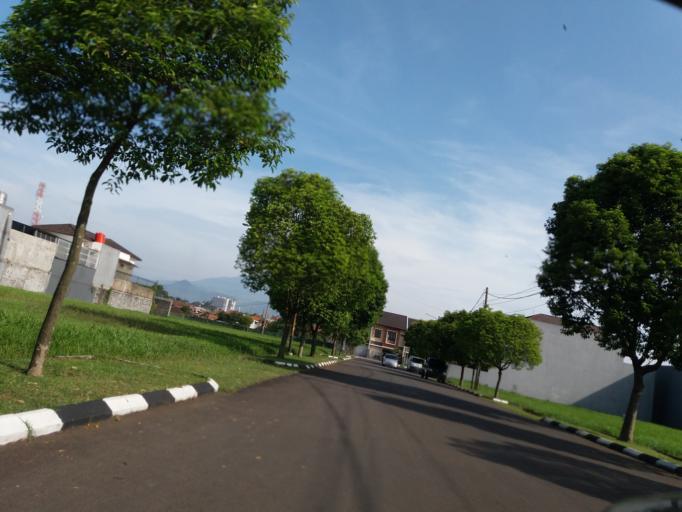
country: ID
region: West Java
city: Bandung
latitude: -6.9593
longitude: 107.6335
